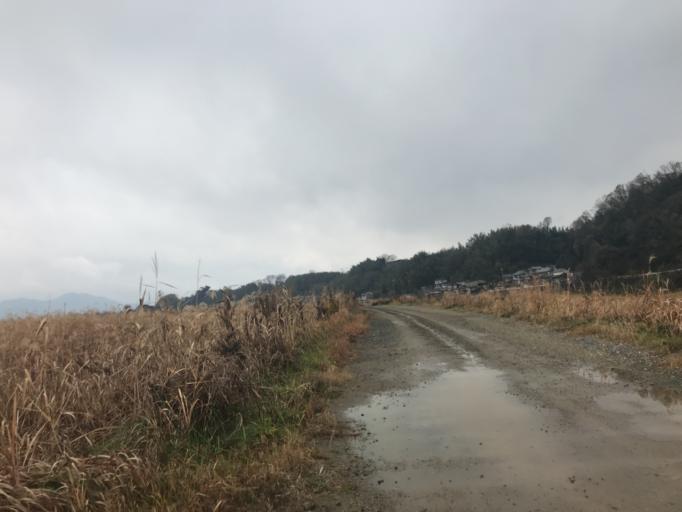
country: JP
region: Kyoto
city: Kameoka
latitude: 35.0174
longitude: 135.6000
